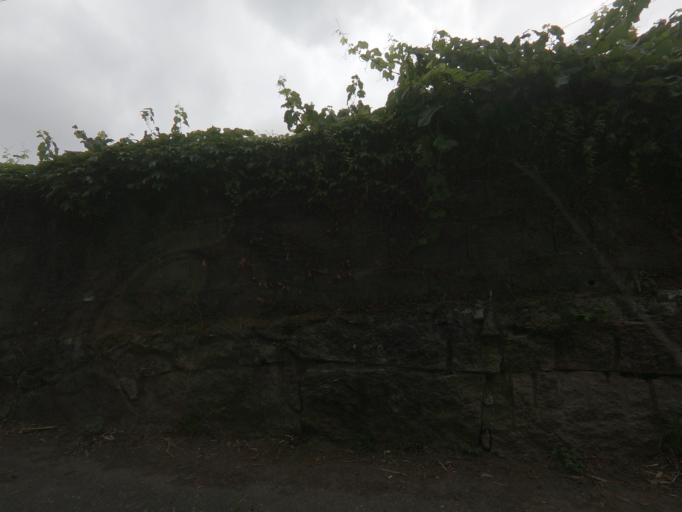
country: ES
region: Galicia
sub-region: Provincia de Pontevedra
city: Tui
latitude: 42.0431
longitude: -8.6569
